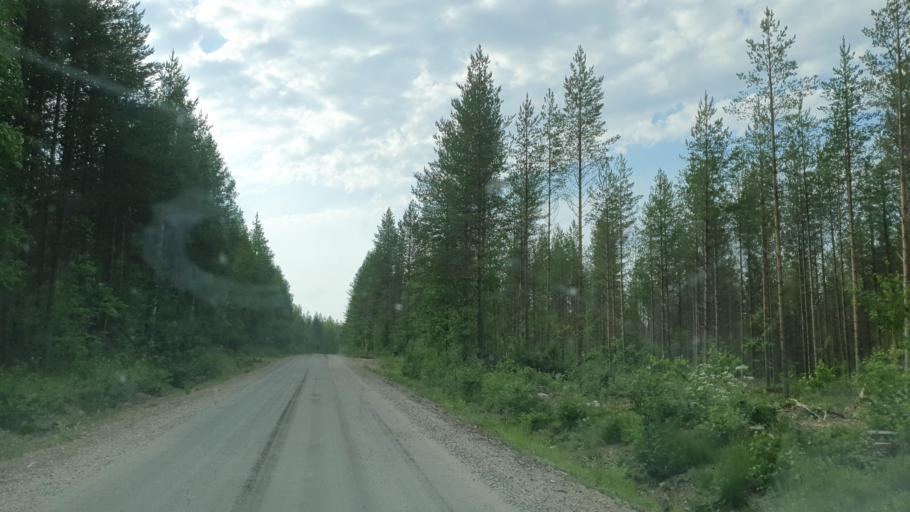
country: FI
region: Kainuu
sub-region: Kehys-Kainuu
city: Kuhmo
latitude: 64.0707
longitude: 29.7389
